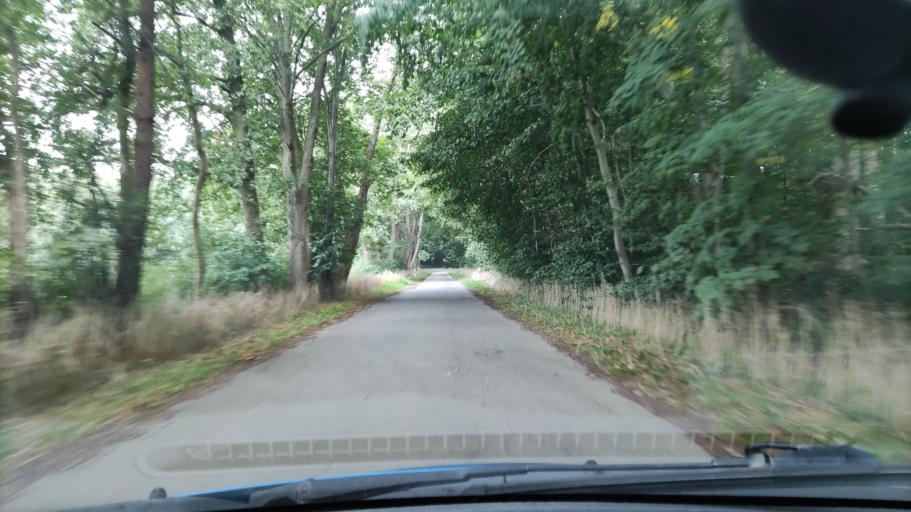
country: DE
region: Lower Saxony
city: Altenmedingen
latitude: 53.1448
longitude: 10.5862
